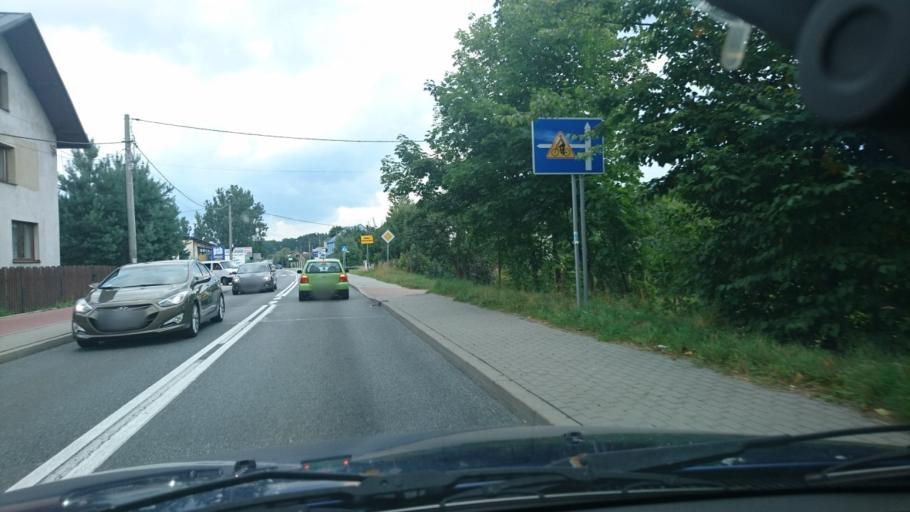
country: PL
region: Silesian Voivodeship
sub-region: Powiat zywiecki
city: Milowka
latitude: 49.5705
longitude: 19.0937
